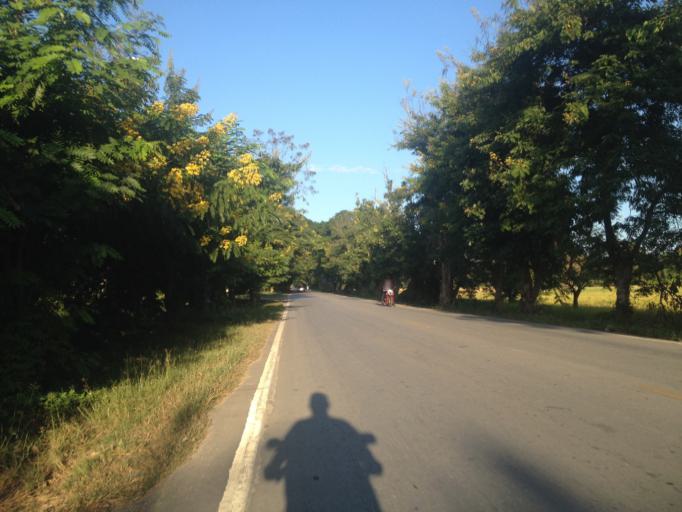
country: TH
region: Chiang Mai
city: San Pa Tong
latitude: 18.6159
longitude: 98.8619
